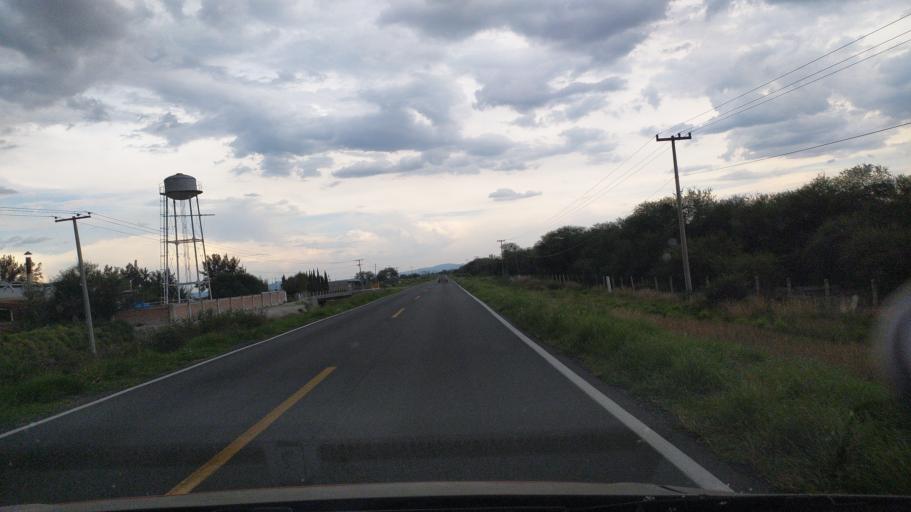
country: MX
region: Guanajuato
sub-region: San Francisco del Rincon
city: San Ignacio de Hidalgo
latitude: 20.8451
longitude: -101.8964
